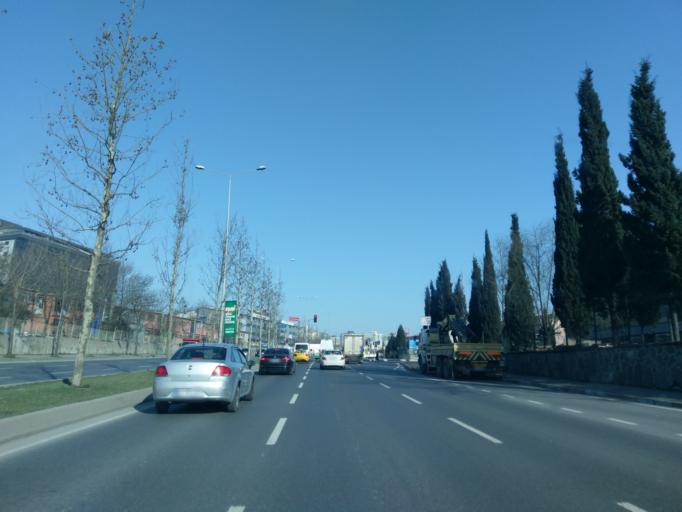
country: TR
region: Istanbul
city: Basaksehir
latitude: 41.0940
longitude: 28.7936
